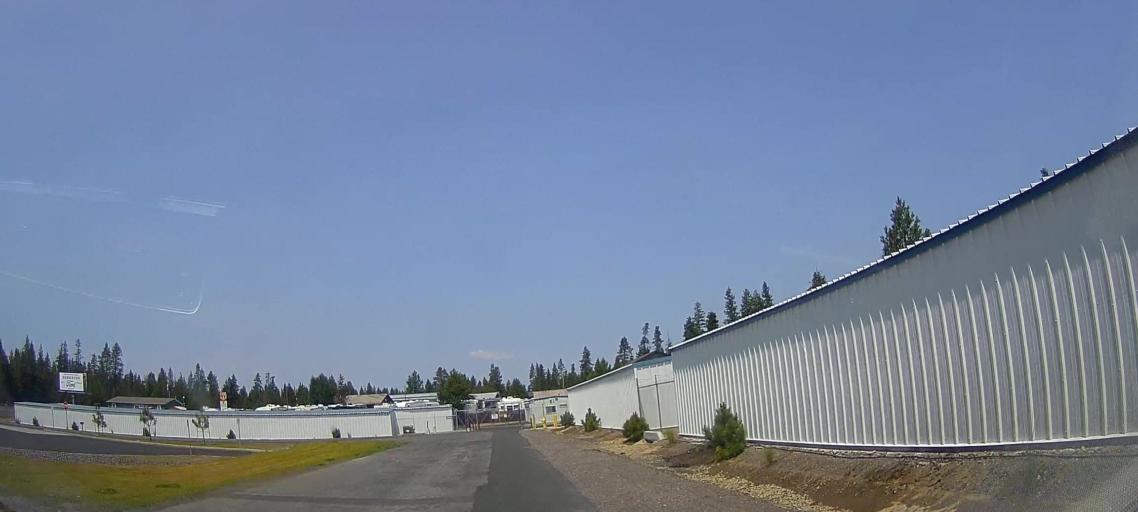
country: US
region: Oregon
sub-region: Deschutes County
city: La Pine
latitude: 43.7113
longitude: -121.4731
